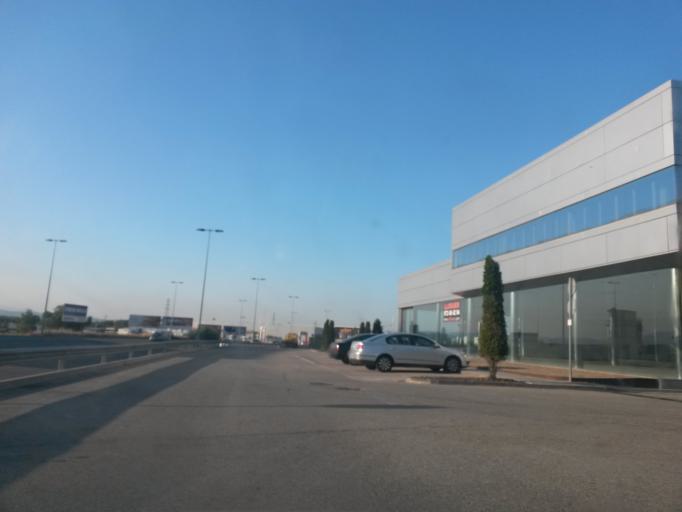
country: ES
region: Catalonia
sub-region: Provincia de Girona
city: Fornells de la Selva
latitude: 41.9320
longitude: 2.7956
